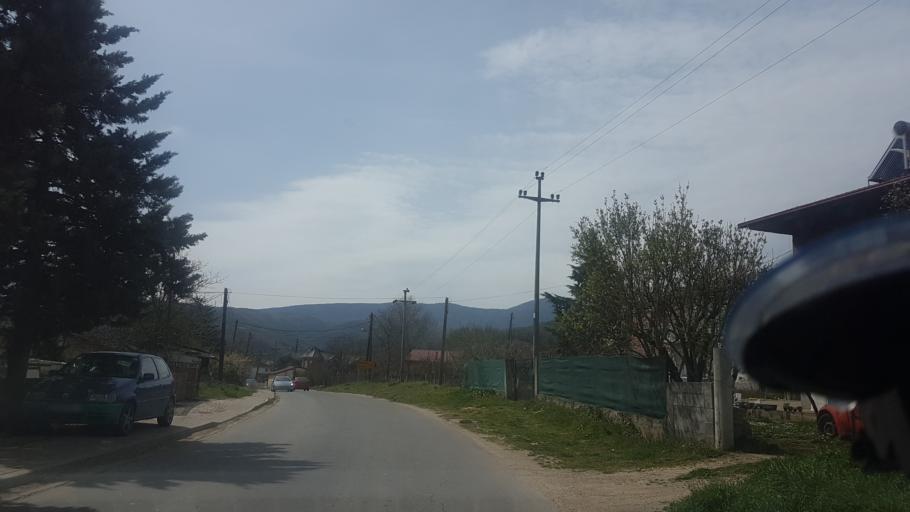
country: MK
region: Zelenikovo
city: Zelenikovo
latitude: 41.8903
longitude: 21.5879
